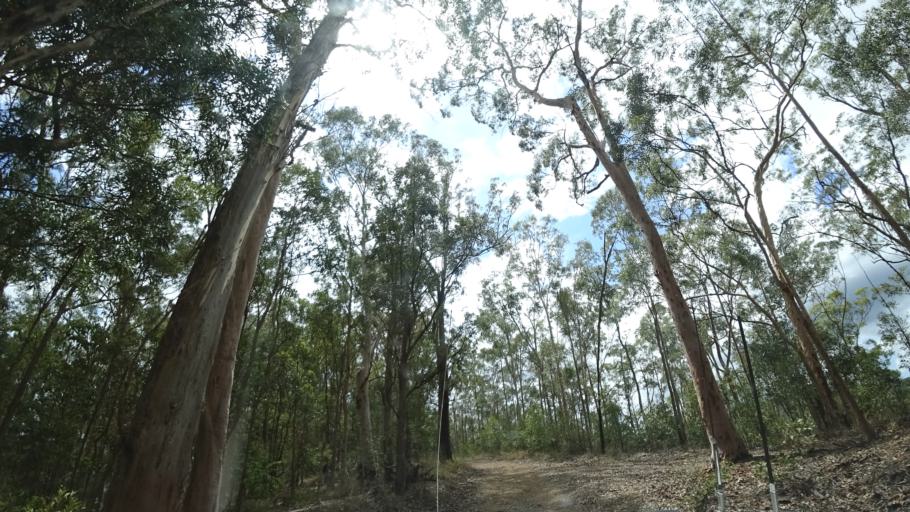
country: AU
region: Queensland
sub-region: Moreton Bay
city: Highvale
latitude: -27.4047
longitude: 152.7408
